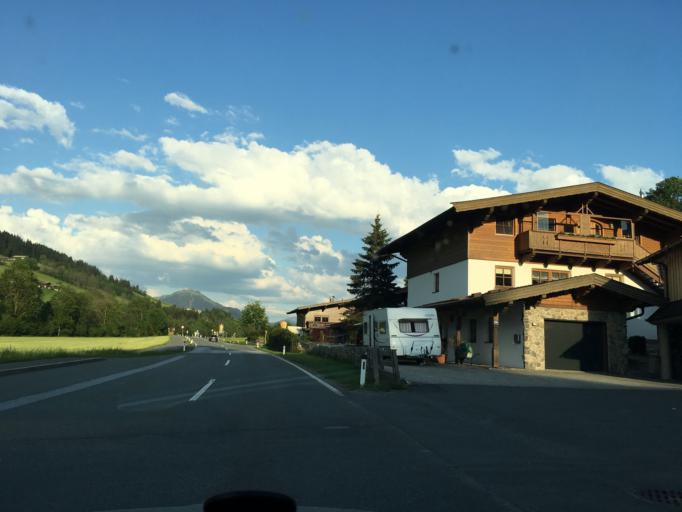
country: AT
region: Tyrol
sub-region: Politischer Bezirk Kitzbuhel
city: Sankt Johann in Tirol
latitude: 47.5083
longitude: 12.4665
